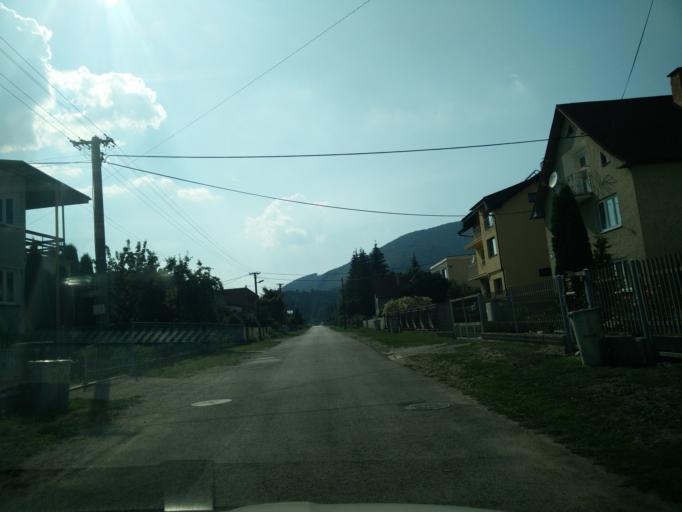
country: SK
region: Zilinsky
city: Rajec
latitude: 49.1303
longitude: 18.6999
